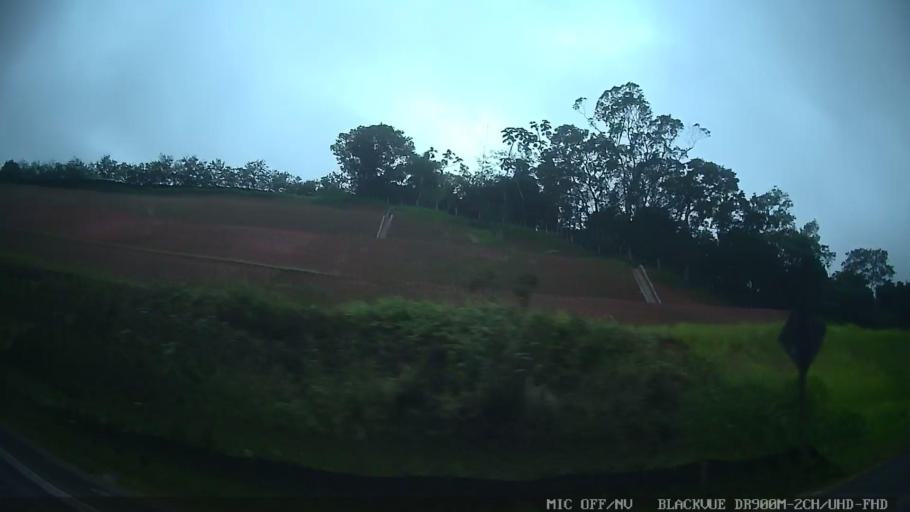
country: BR
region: Sao Paulo
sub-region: Aruja
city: Aruja
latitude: -23.4074
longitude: -46.2980
